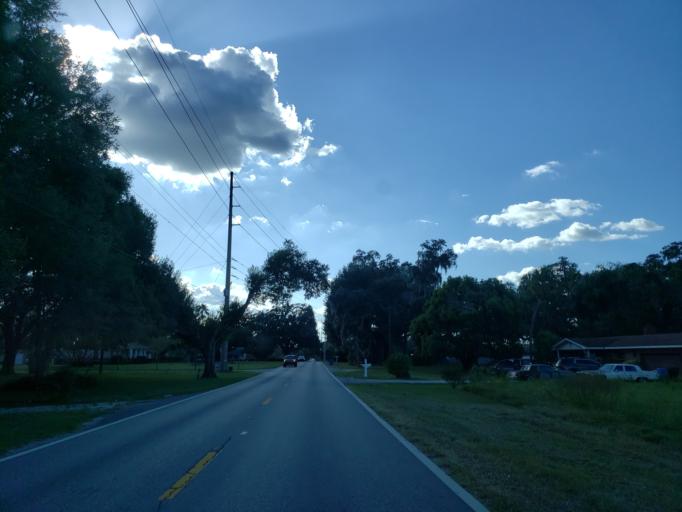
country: US
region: Florida
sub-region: Hillsborough County
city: Dover
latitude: 27.9670
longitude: -82.2107
